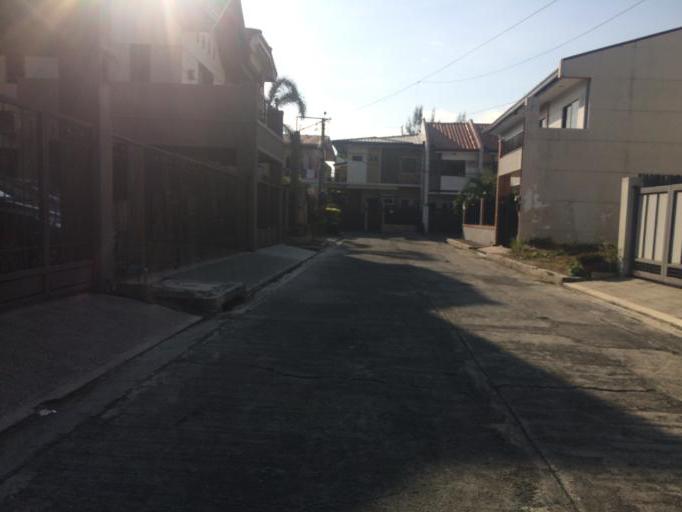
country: PH
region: Calabarzon
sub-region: Province of Rizal
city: Taytay
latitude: 14.5544
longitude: 121.1065
